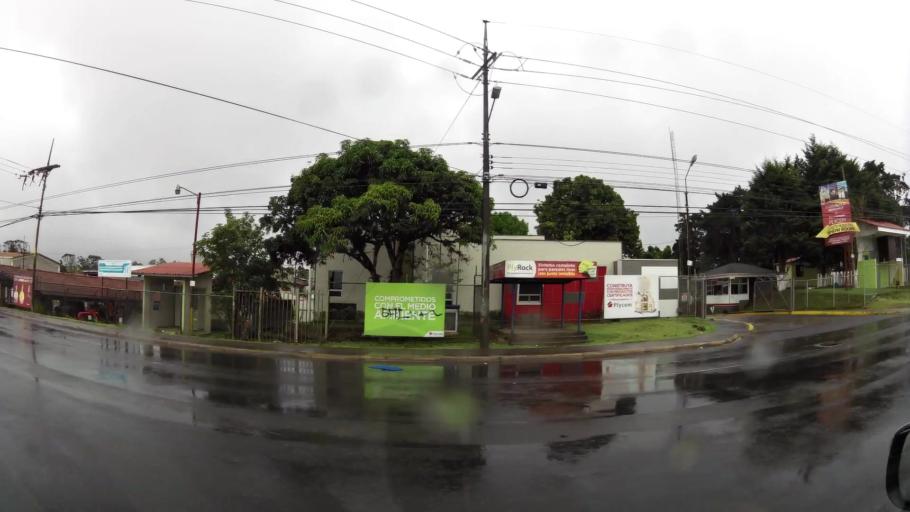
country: CR
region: Cartago
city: Paraiso
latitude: 9.8442
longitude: -83.8871
